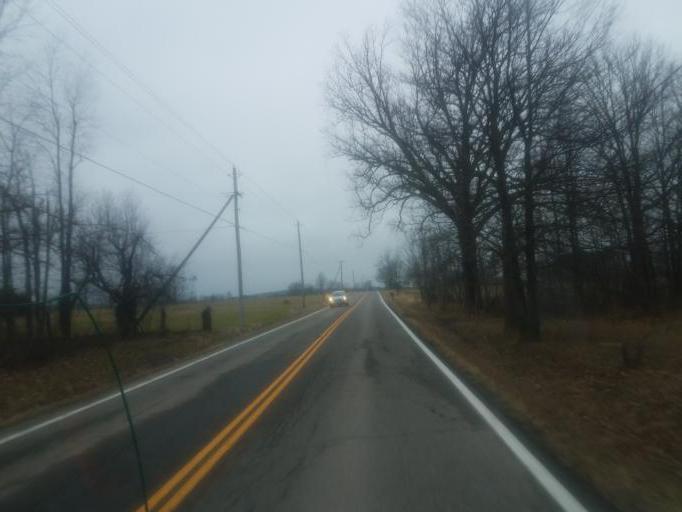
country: US
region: Ohio
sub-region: Richland County
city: Lincoln Heights
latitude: 40.8990
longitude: -82.4647
